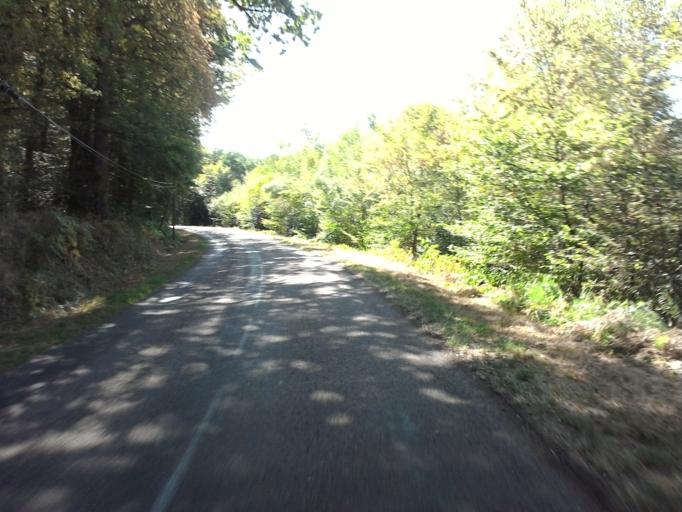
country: FR
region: Bourgogne
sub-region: Departement de la Nievre
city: Lormes
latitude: 47.2683
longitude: 3.9583
